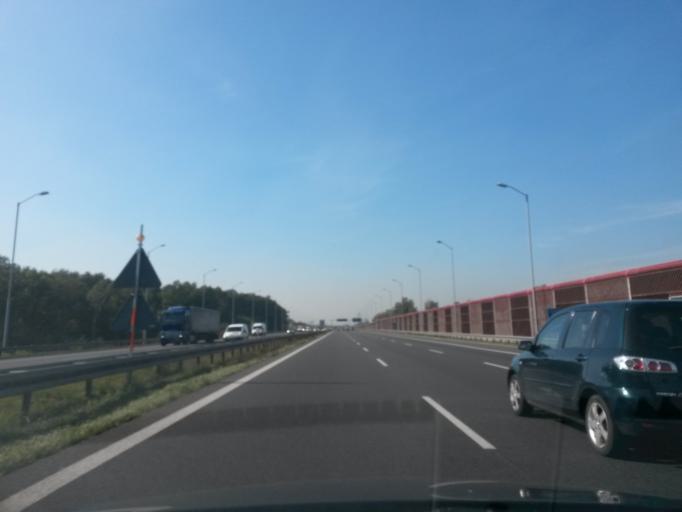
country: PL
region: Silesian Voivodeship
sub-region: Ruda Slaska
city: Ruda Slaska
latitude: 50.2542
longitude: 18.8675
